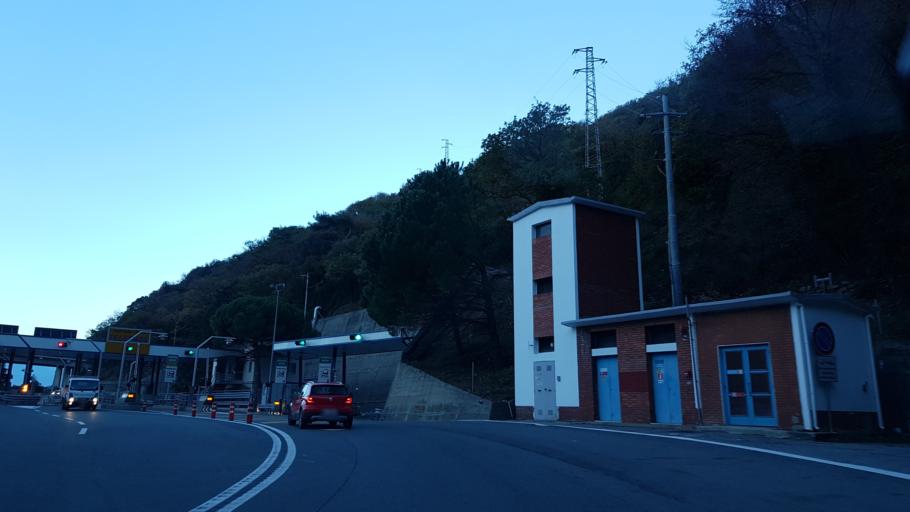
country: IT
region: Liguria
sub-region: Provincia di Genova
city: Bogliasco
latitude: 44.3982
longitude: 9.0149
